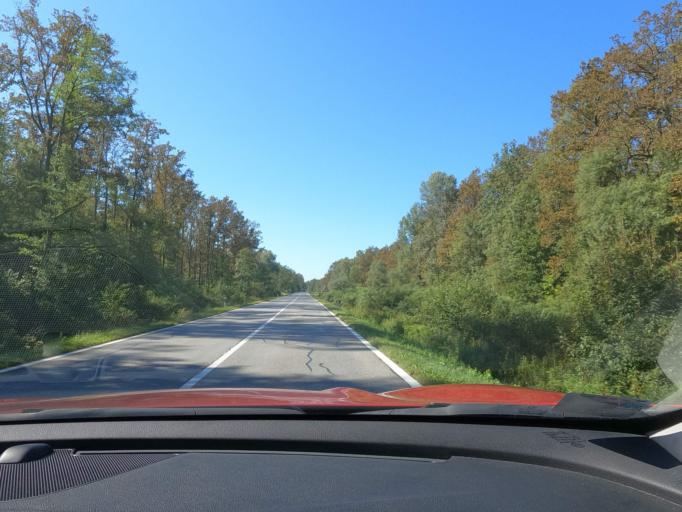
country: HR
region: Sisacko-Moslavacka
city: Budasevo
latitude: 45.5032
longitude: 16.5165
